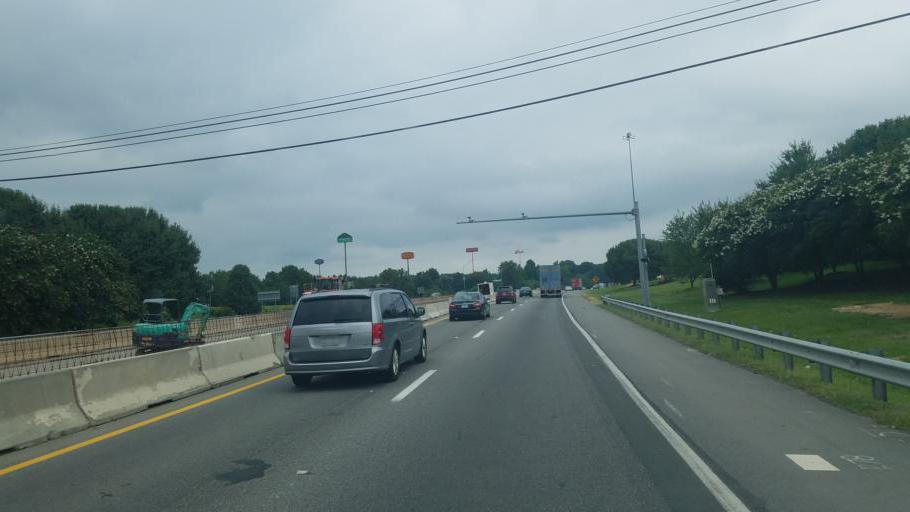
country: US
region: North Carolina
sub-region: Iredell County
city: Mooresville
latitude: 35.5941
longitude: -80.8598
